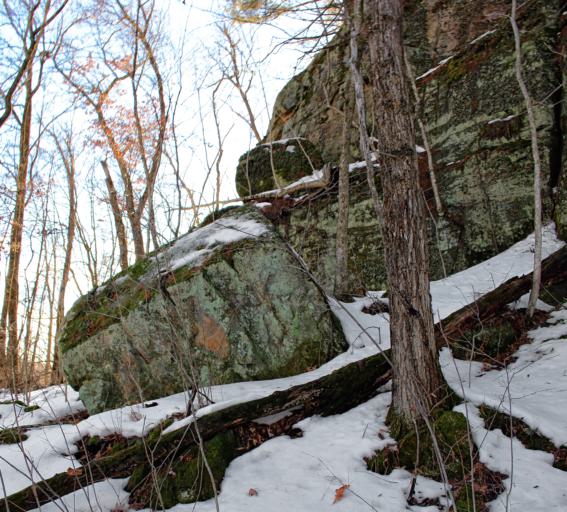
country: US
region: Wisconsin
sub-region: Sauk County
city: Reedsburg
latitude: 43.3554
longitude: -89.9824
